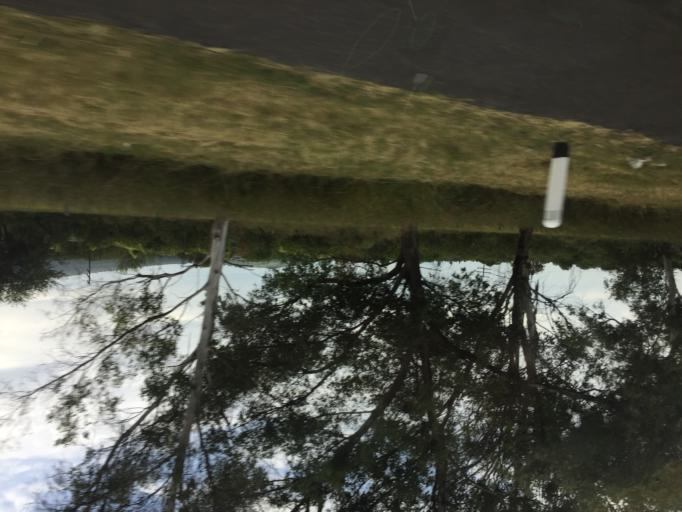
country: MX
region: Jalisco
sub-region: Ocotlan
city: Joconoxtle (La Tuna)
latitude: 20.3767
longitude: -102.6765
